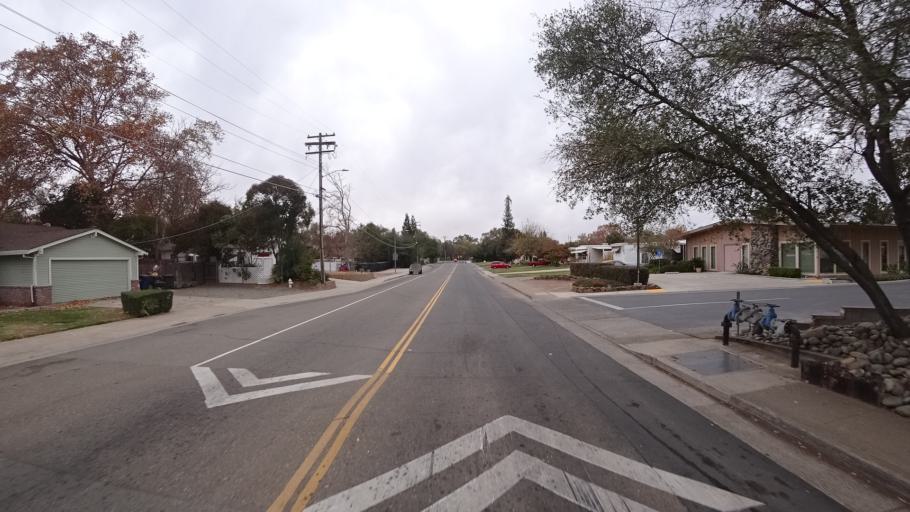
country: US
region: California
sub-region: Sacramento County
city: Citrus Heights
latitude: 38.7052
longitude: -121.2964
